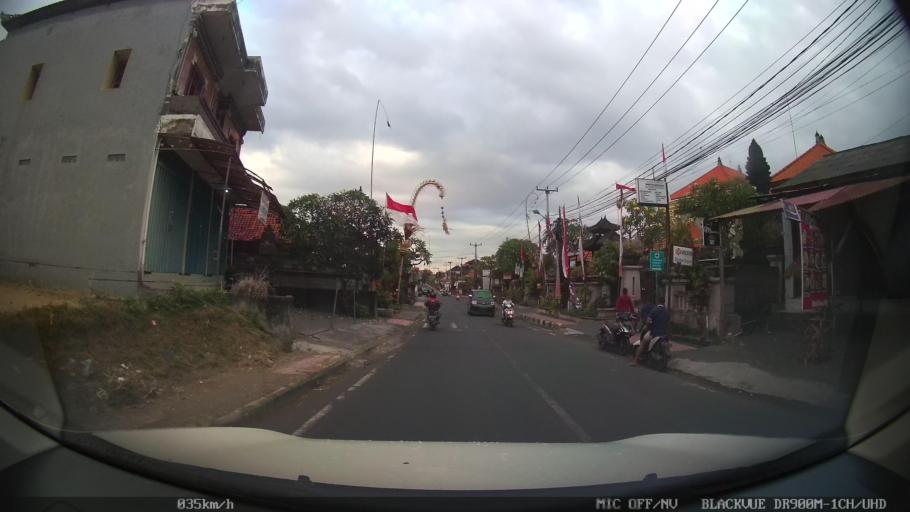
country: ID
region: Bali
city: Banjar Pasekan
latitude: -8.6329
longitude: 115.2842
